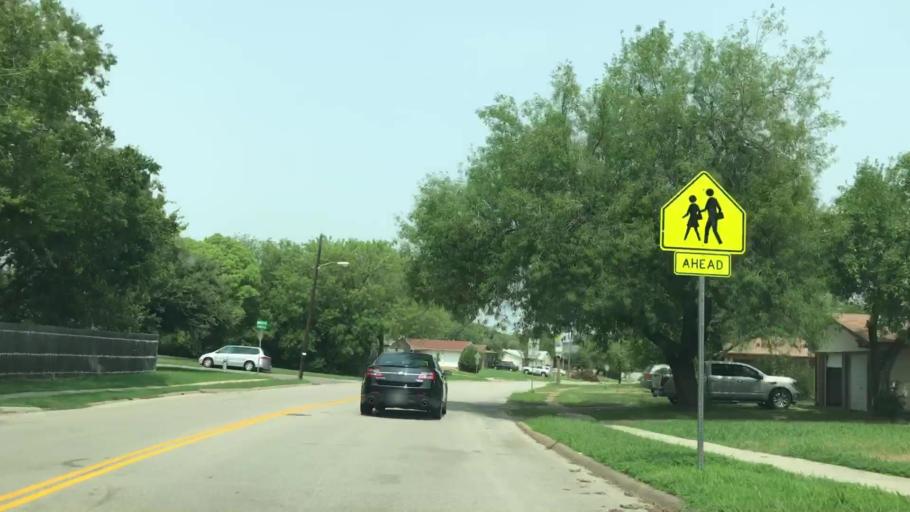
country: US
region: Texas
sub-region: Dallas County
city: Irving
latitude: 32.8424
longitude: -97.0054
